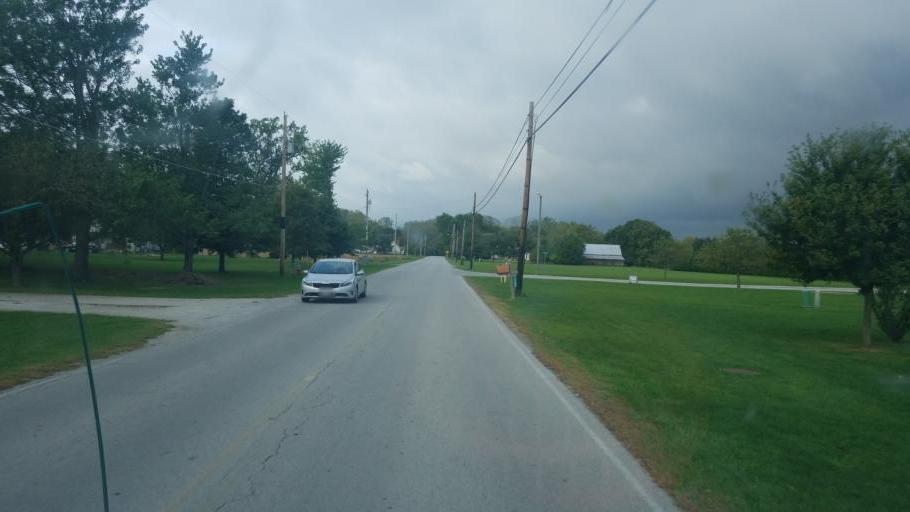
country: US
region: Ohio
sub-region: Wood County
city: North Baltimore
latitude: 41.1825
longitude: -83.6559
